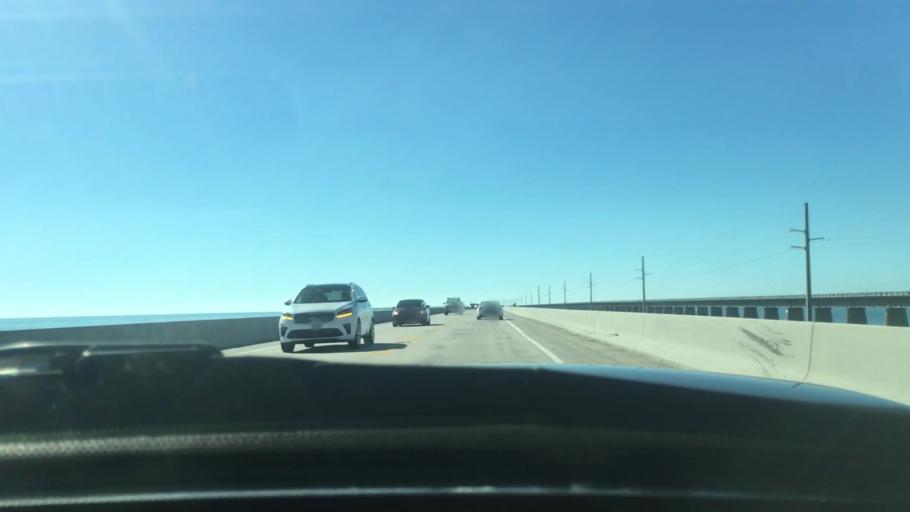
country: US
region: Florida
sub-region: Monroe County
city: Marathon
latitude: 24.6951
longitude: -81.1831
